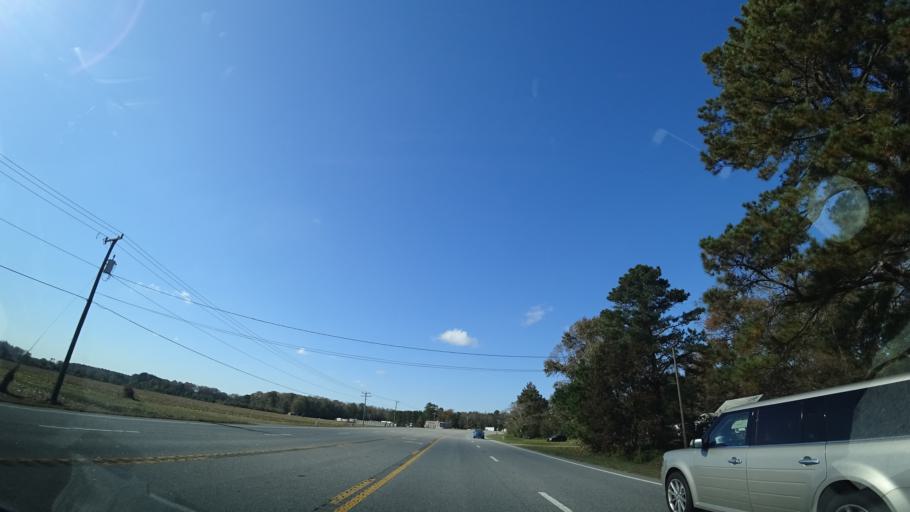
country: US
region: North Carolina
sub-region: Currituck County
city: Currituck
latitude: 36.4590
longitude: -76.0976
